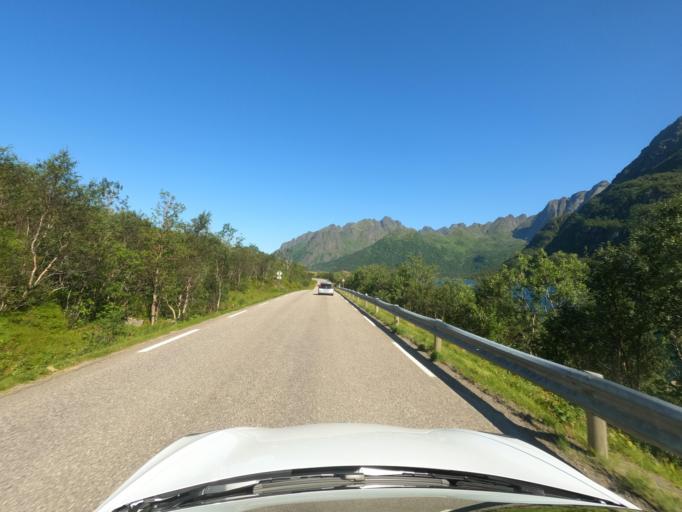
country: NO
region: Nordland
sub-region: Hadsel
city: Melbu
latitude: 68.3894
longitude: 14.8300
